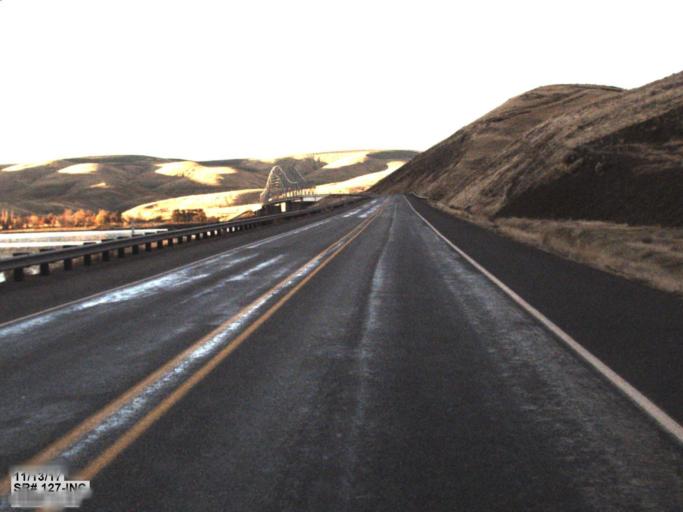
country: US
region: Washington
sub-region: Garfield County
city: Pomeroy
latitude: 46.6199
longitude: -117.7941
